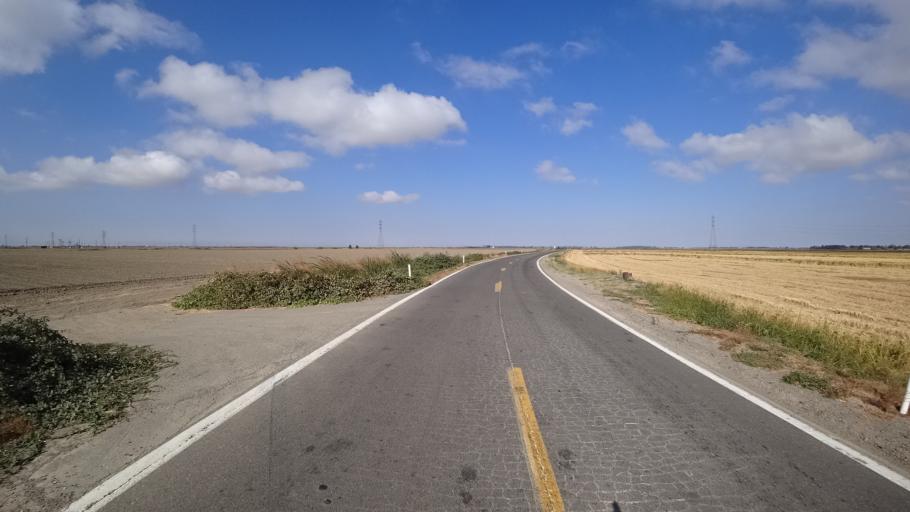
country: US
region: California
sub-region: Yolo County
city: Woodland
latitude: 38.8109
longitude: -121.7357
